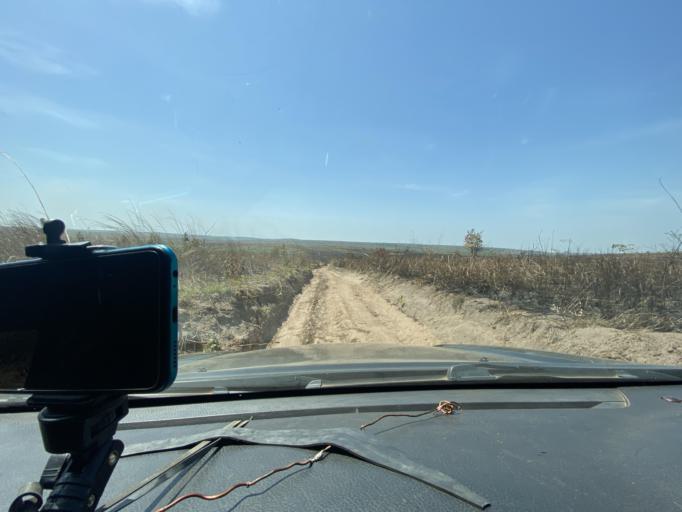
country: CD
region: Kasai-Oriental
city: Kabinda
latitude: -5.9405
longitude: 24.8082
